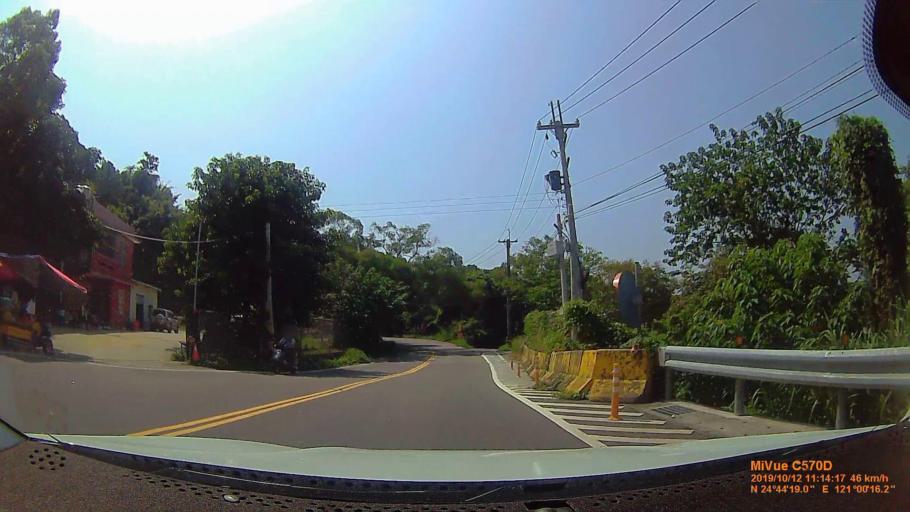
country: TW
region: Taiwan
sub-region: Hsinchu
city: Hsinchu
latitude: 24.7385
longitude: 121.0044
